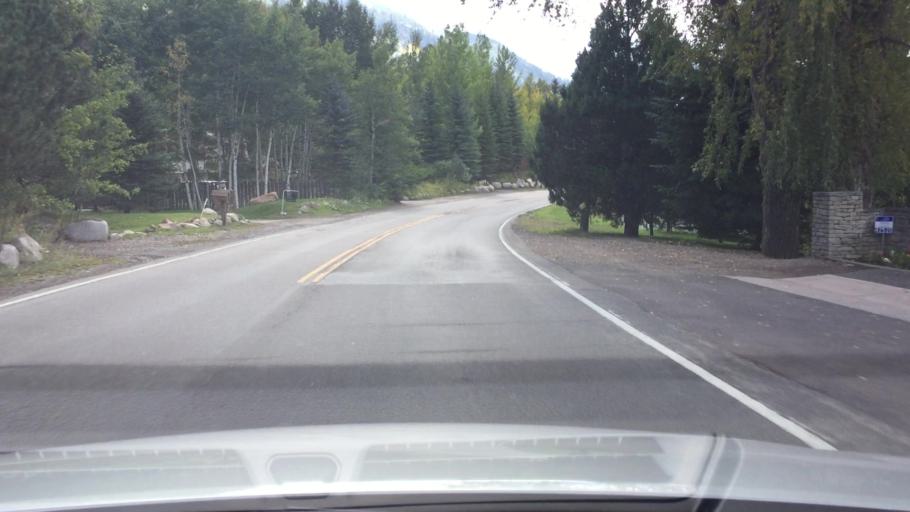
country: US
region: Colorado
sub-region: Pitkin County
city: Aspen
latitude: 39.1806
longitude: -106.8016
